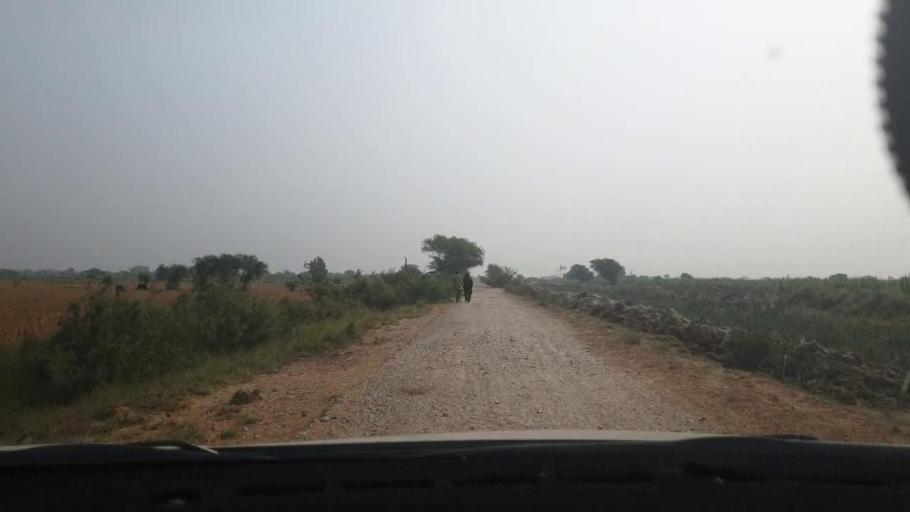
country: PK
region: Sindh
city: Tando Muhammad Khan
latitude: 25.0704
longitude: 68.5030
